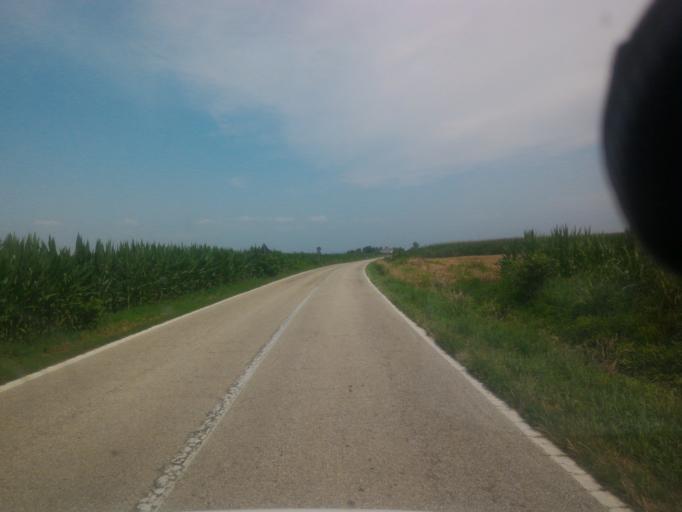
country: IT
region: Piedmont
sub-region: Provincia di Torino
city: Buriasco
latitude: 44.8601
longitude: 7.4263
